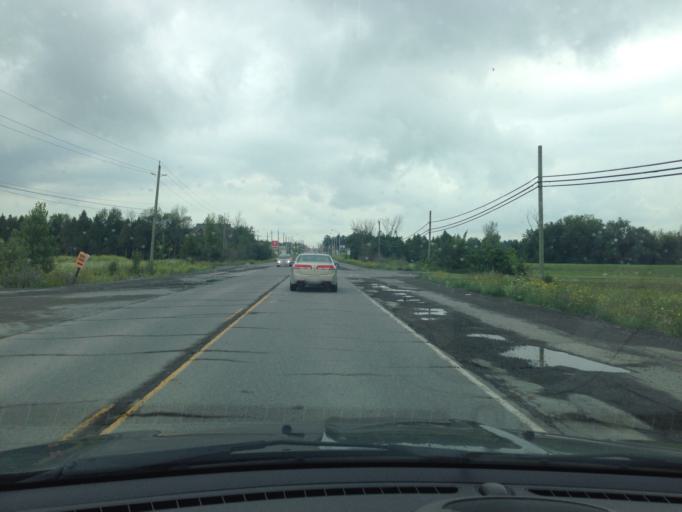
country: CA
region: Ontario
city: Ottawa
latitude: 45.3150
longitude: -75.5905
